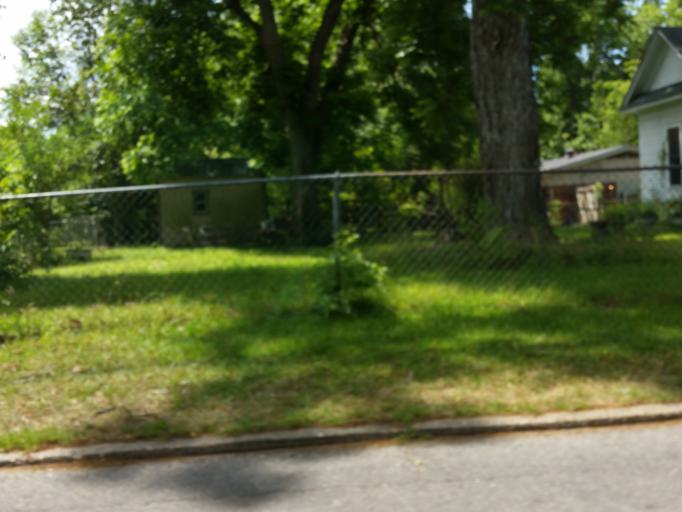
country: US
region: Mississippi
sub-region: Lauderdale County
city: Meridian
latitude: 32.3853
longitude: -88.7181
